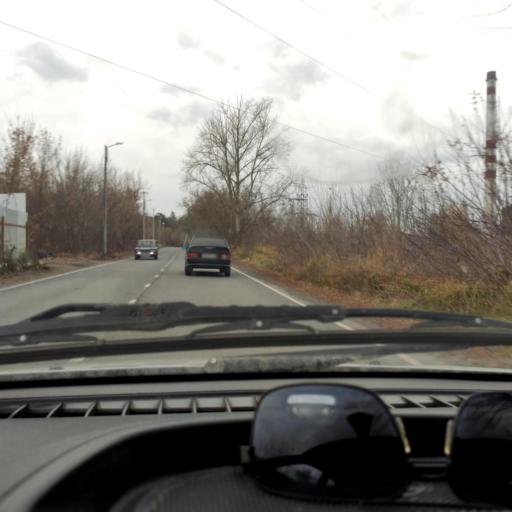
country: RU
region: Samara
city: Zhigulevsk
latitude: 53.5141
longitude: 49.4705
